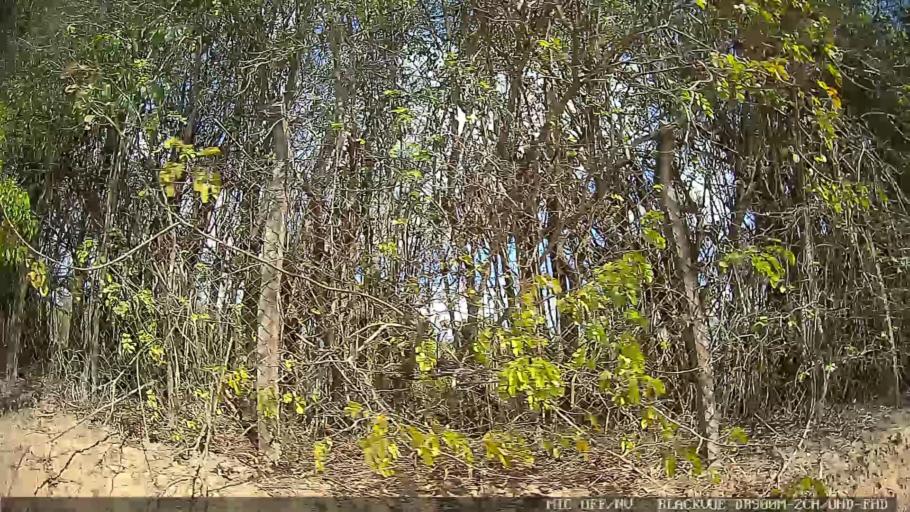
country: BR
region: Sao Paulo
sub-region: Itupeva
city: Itupeva
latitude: -23.2361
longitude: -47.0581
